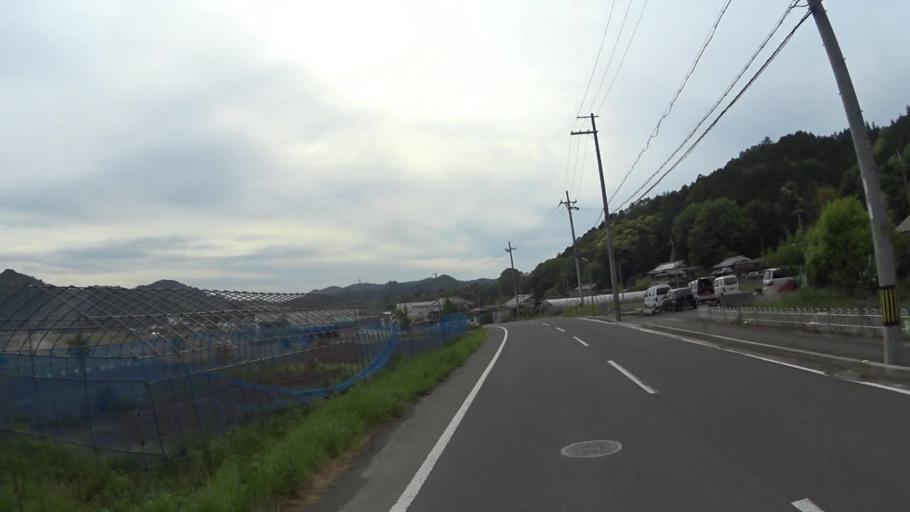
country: JP
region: Kyoto
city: Kameoka
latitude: 35.1004
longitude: 135.5411
